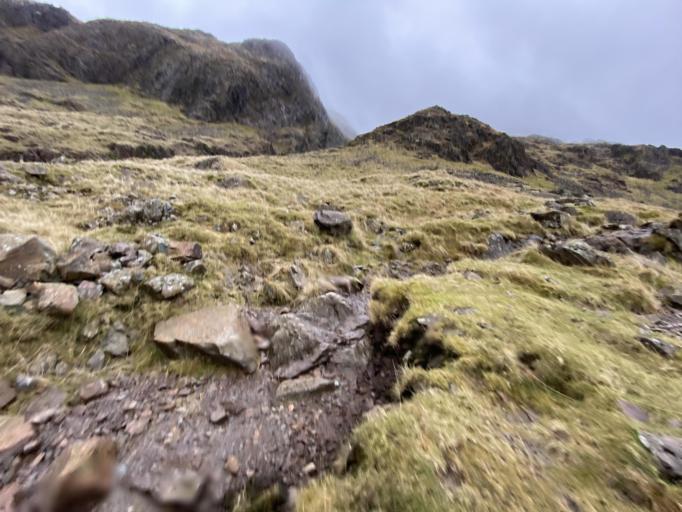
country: GB
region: England
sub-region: Cumbria
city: Keswick
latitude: 54.4710
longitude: -3.2036
